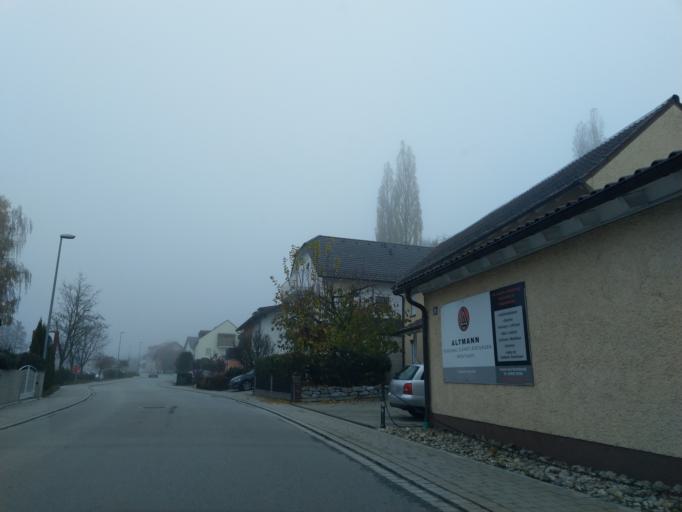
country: DE
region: Bavaria
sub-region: Lower Bavaria
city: Hengersberg
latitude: 48.7765
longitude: 13.0503
